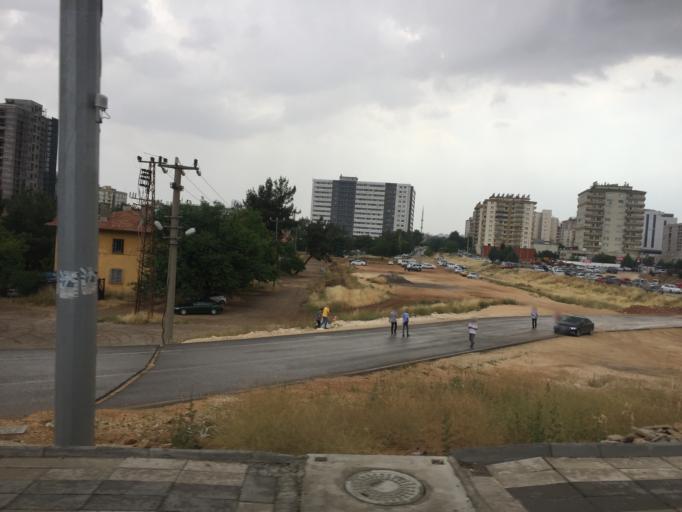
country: TR
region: Gaziantep
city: Gaziantep
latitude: 37.0738
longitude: 37.3722
